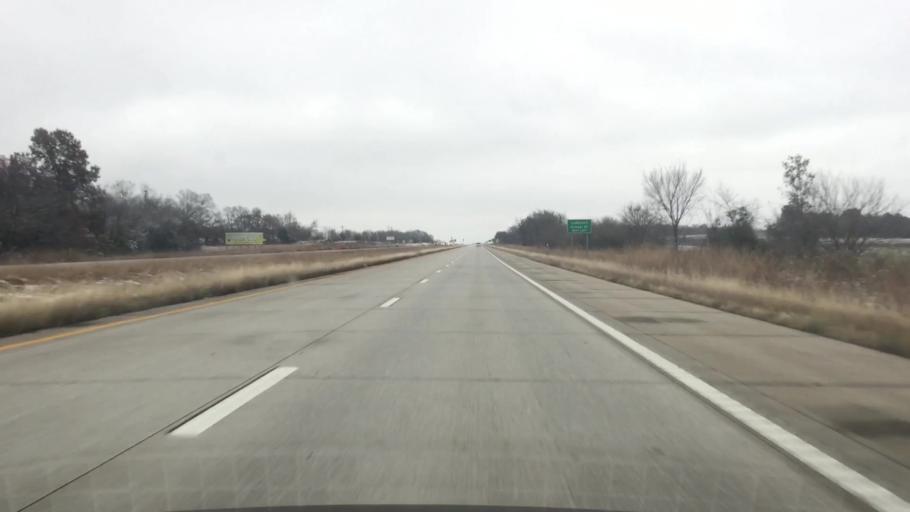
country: US
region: Missouri
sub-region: Henry County
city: Clinton
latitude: 38.2095
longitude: -93.7561
